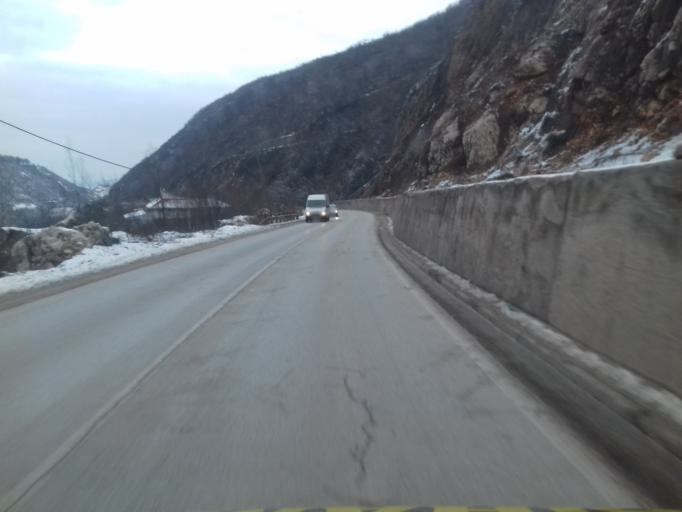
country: BA
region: Republika Srpska
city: Pale
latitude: 43.8425
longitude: 18.4779
